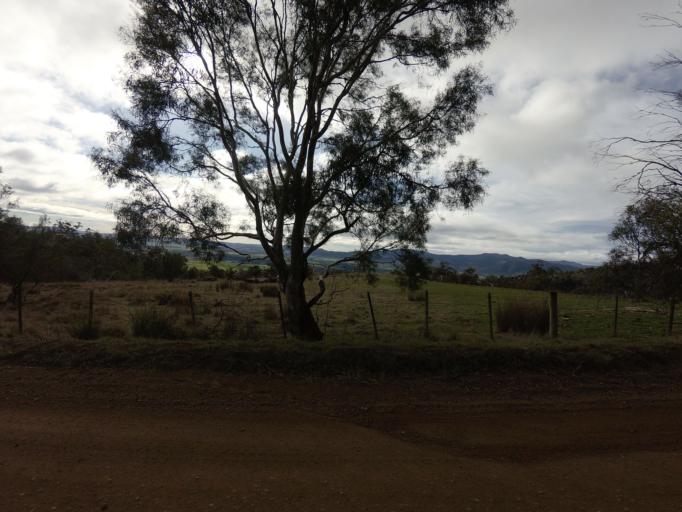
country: AU
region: Tasmania
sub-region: Derwent Valley
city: New Norfolk
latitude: -42.7325
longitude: 146.8685
